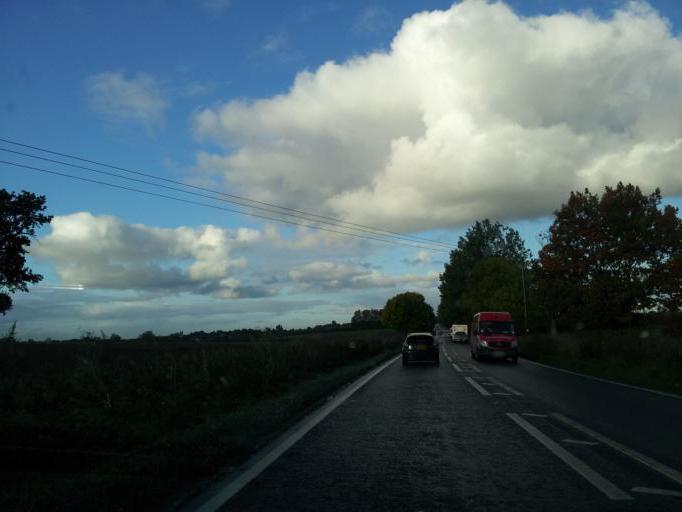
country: GB
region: England
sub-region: Norfolk
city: Lingwood
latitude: 52.6362
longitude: 1.4746
